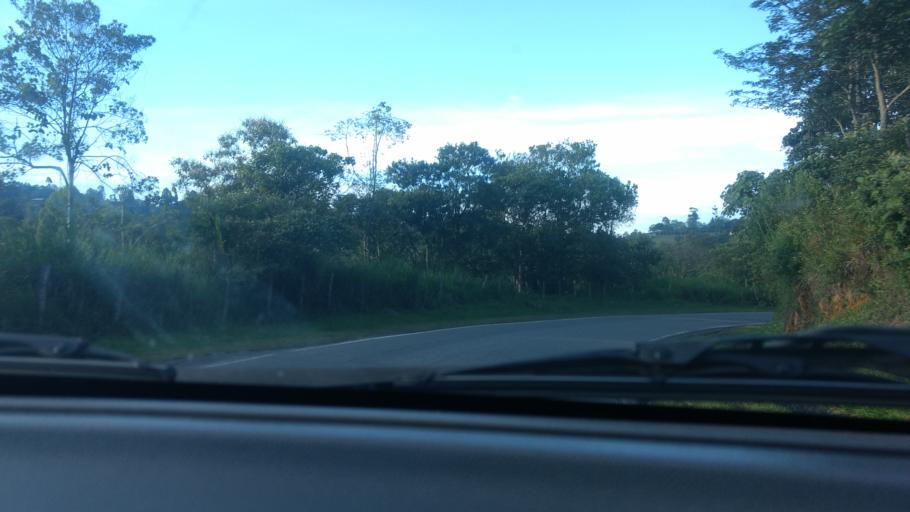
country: CO
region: Cauca
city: Rosas
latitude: 2.3410
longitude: -76.6923
